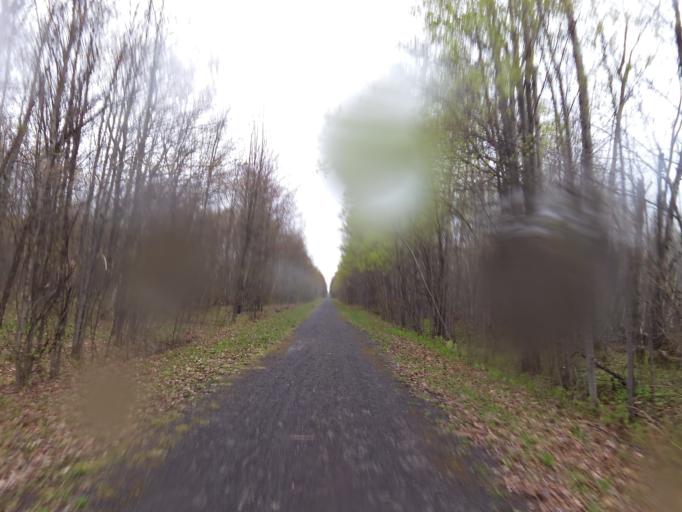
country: CA
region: Ontario
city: Bourget
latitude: 45.4327
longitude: -75.2620
